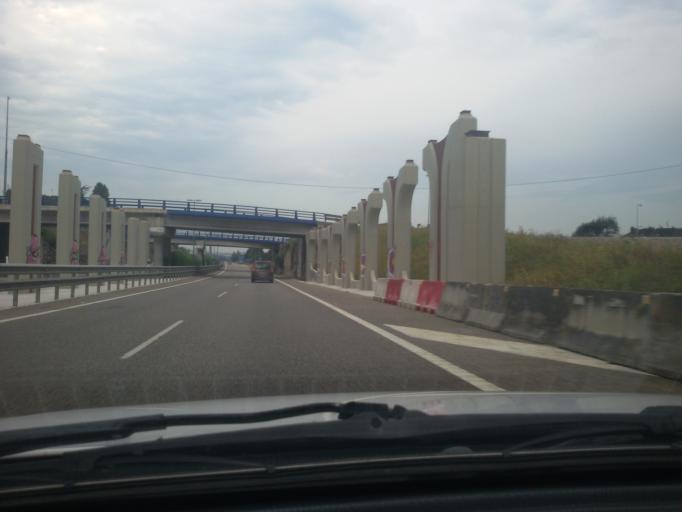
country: ES
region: Asturias
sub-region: Province of Asturias
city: Lugones
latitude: 43.3849
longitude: -5.8298
